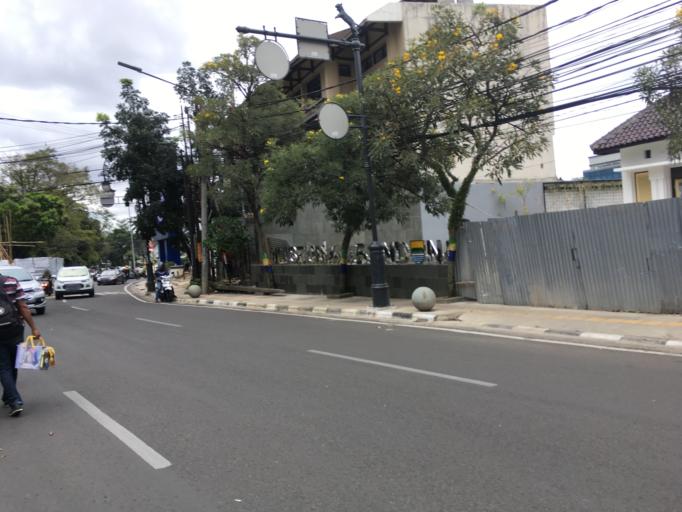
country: ID
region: West Java
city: Bandung
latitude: -6.9102
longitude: 107.6095
